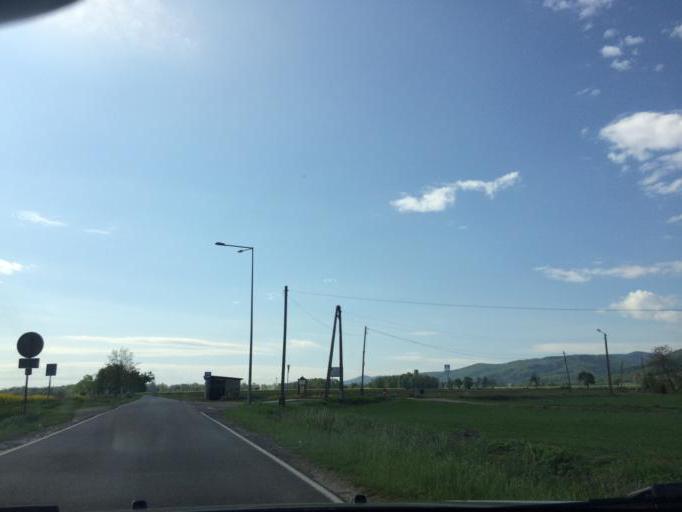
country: PL
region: Lower Silesian Voivodeship
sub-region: Powiat dzierzoniowski
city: Pieszyce
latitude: 50.7291
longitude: 16.5647
